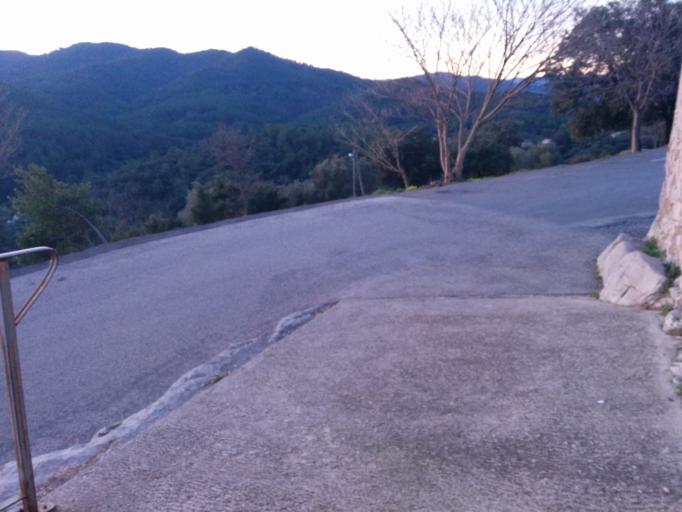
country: FR
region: Languedoc-Roussillon
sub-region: Departement du Gard
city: Ales
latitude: 44.1234
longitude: 4.0634
